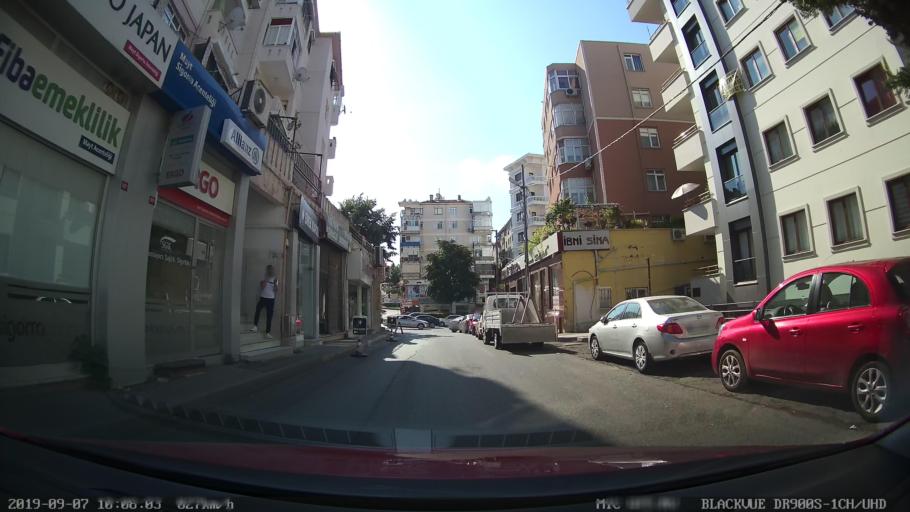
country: TR
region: Istanbul
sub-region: Atasehir
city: Atasehir
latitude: 40.9482
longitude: 29.1127
